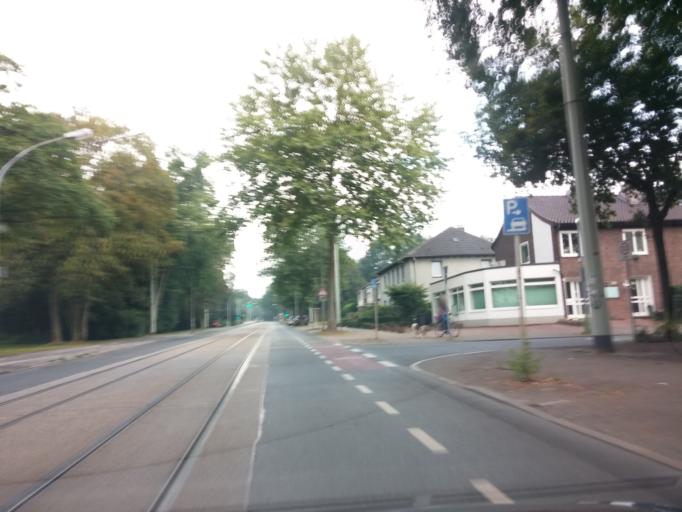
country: DE
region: North Rhine-Westphalia
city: Herten
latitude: 51.5703
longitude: 7.0782
